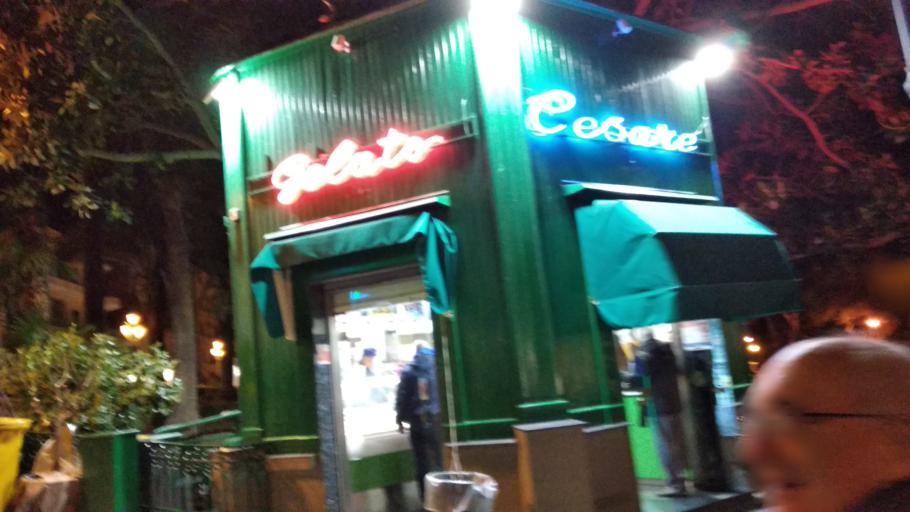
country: IT
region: Calabria
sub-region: Provincia di Reggio Calabria
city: Reggio Calabria
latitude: 38.1143
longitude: 15.6503
